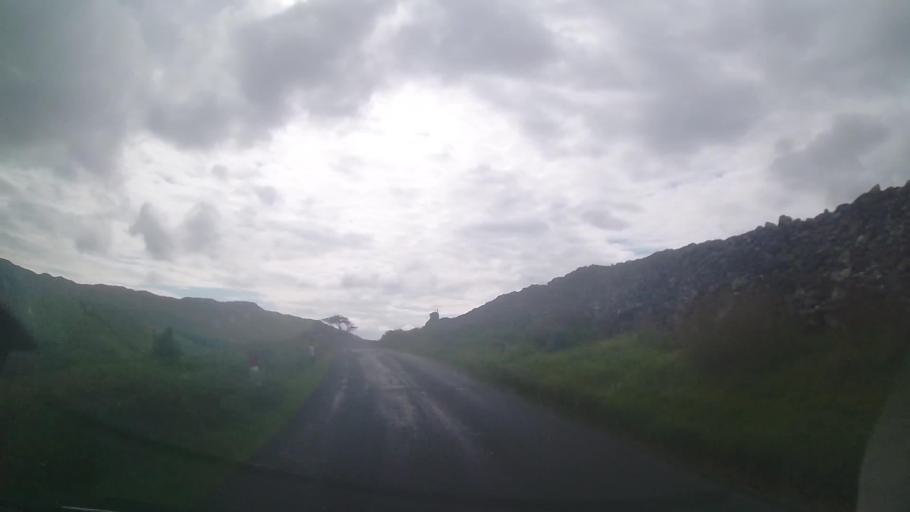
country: GB
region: England
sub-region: Cumbria
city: Ambleside
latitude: 54.4503
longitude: -2.9389
